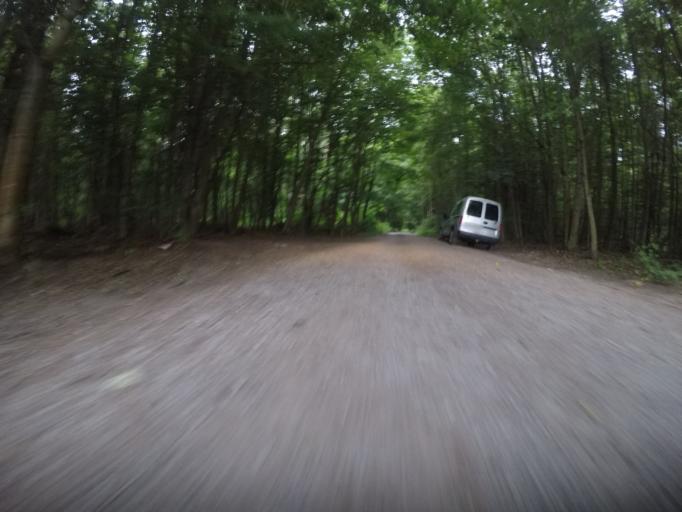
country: DE
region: Baden-Wuerttemberg
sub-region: Regierungsbezirk Stuttgart
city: Eberdingen
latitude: 48.8711
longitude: 8.9929
